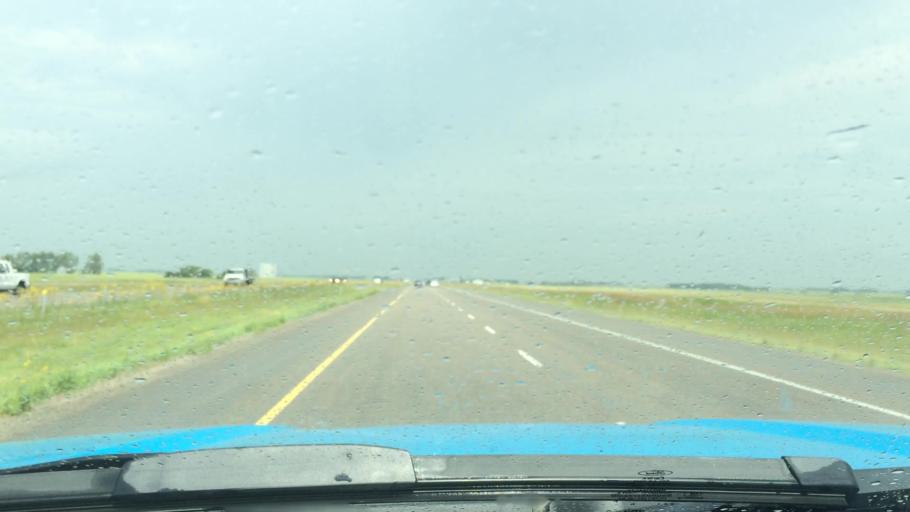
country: CA
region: Alberta
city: Didsbury
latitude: 51.6847
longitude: -114.0254
